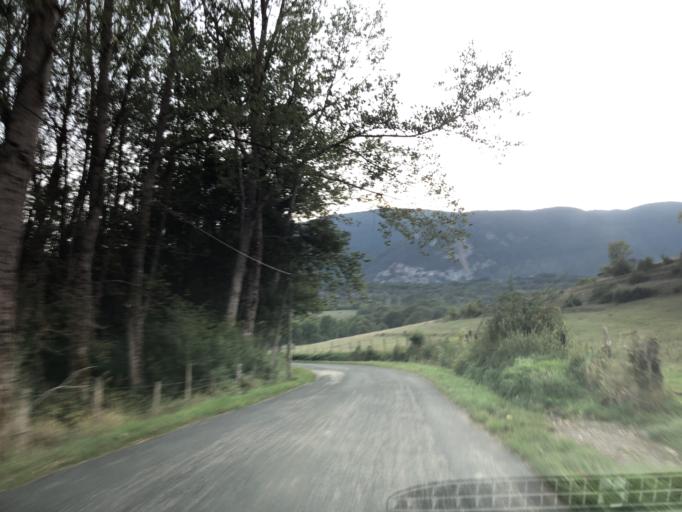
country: FR
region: Rhone-Alpes
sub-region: Departement de l'Ain
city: Virieu-le-Grand
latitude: 45.7963
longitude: 5.6293
